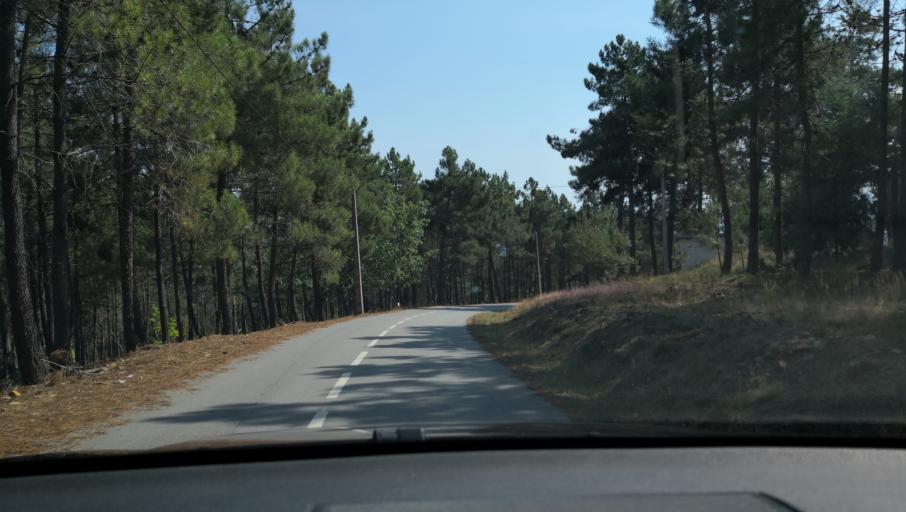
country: PT
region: Vila Real
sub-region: Sabrosa
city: Sabrosa
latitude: 41.2749
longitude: -7.6187
